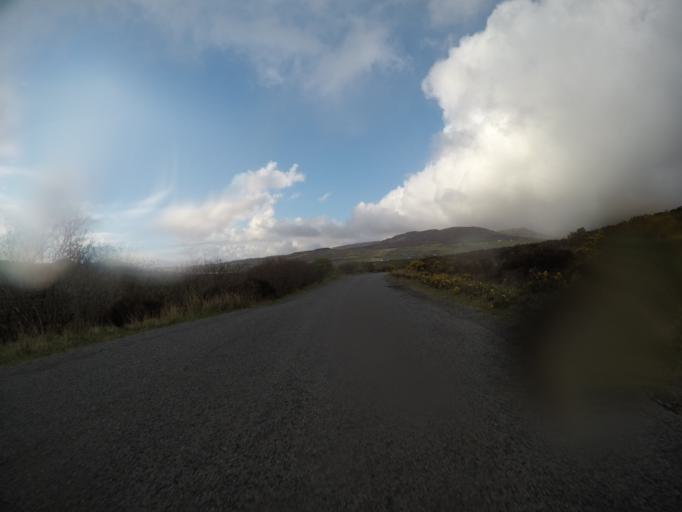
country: GB
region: Scotland
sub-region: Highland
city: Portree
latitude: 57.4700
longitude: -6.2998
